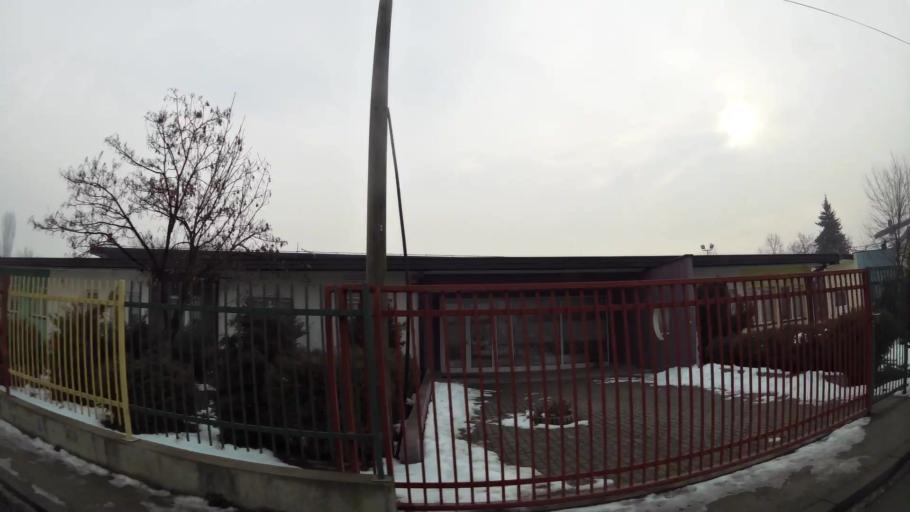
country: MK
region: Ilinden
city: Jurumleri
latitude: 41.9643
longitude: 21.5598
